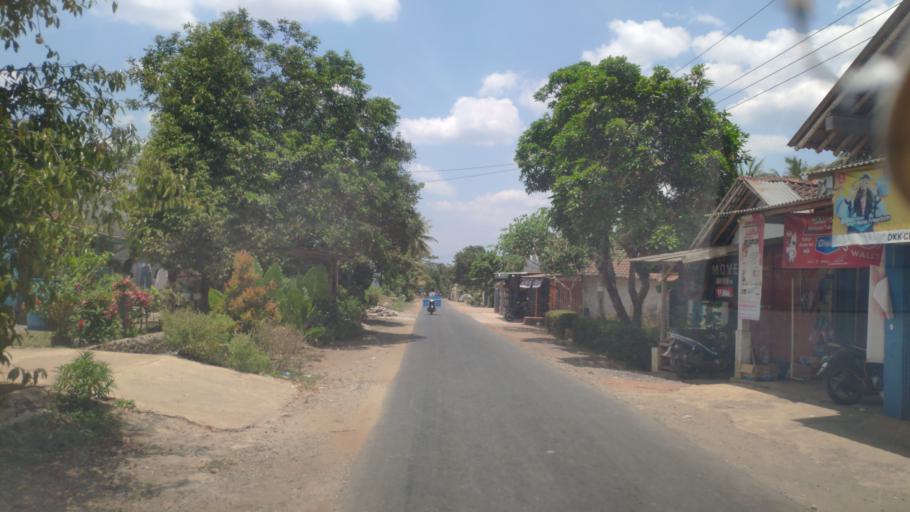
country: ID
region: Central Java
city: Purbalingga
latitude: -7.4260
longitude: 109.5279
